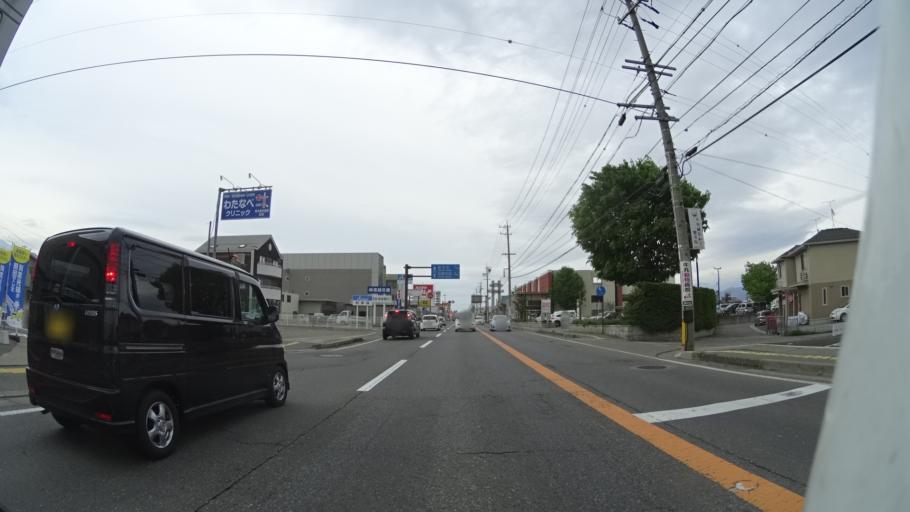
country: JP
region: Nagano
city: Nagano-shi
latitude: 36.6118
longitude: 138.1729
